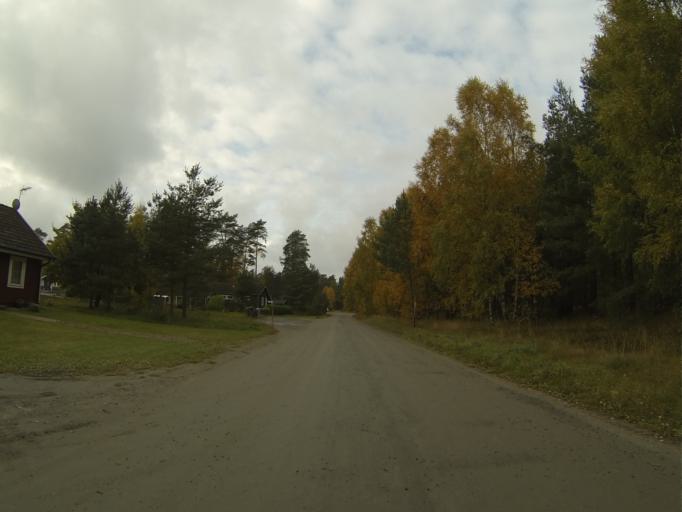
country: SE
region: Skane
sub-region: Sjobo Kommun
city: Blentarp
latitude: 55.6353
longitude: 13.6394
